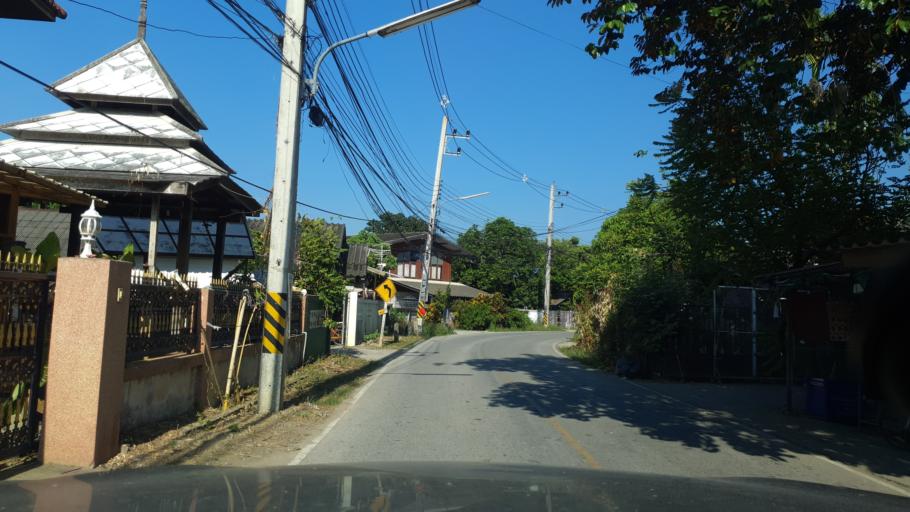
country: TH
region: Chiang Mai
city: Saraphi
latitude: 18.7290
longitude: 99.0624
